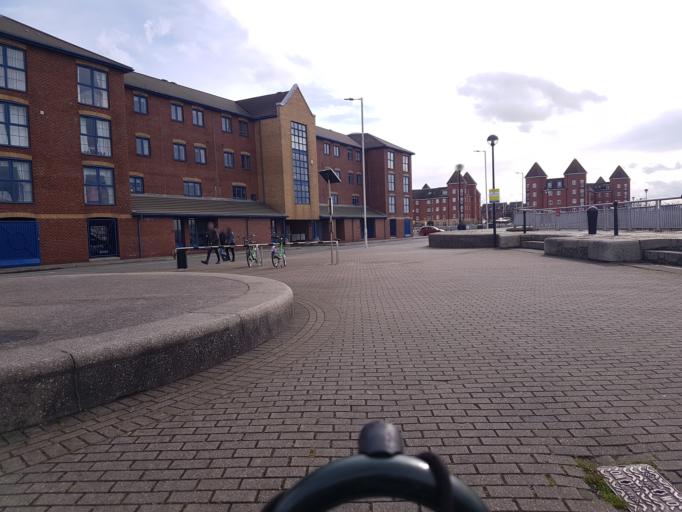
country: GB
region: England
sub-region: Liverpool
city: Liverpool
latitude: 53.3915
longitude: -2.9883
